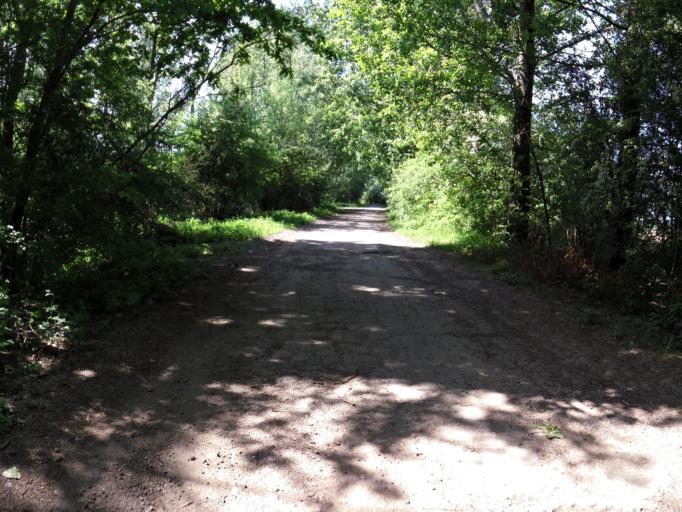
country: NL
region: Gelderland
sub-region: Gemeente Neerijnen
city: Neerijnen
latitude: 51.8158
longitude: 5.3132
